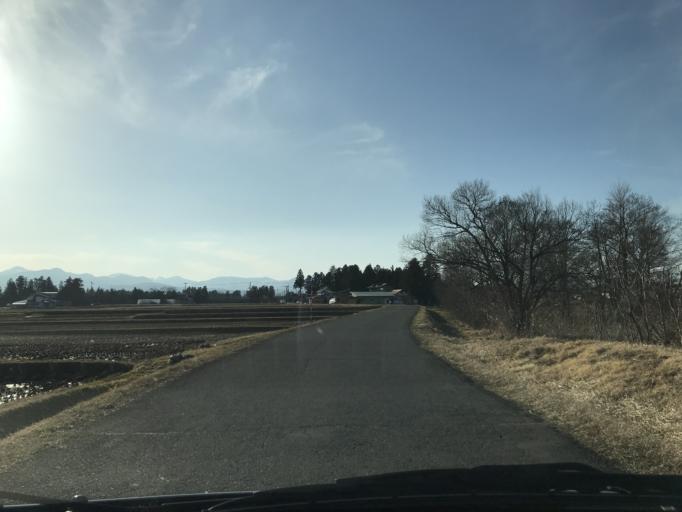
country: JP
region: Iwate
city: Kitakami
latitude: 39.2271
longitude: 141.0879
